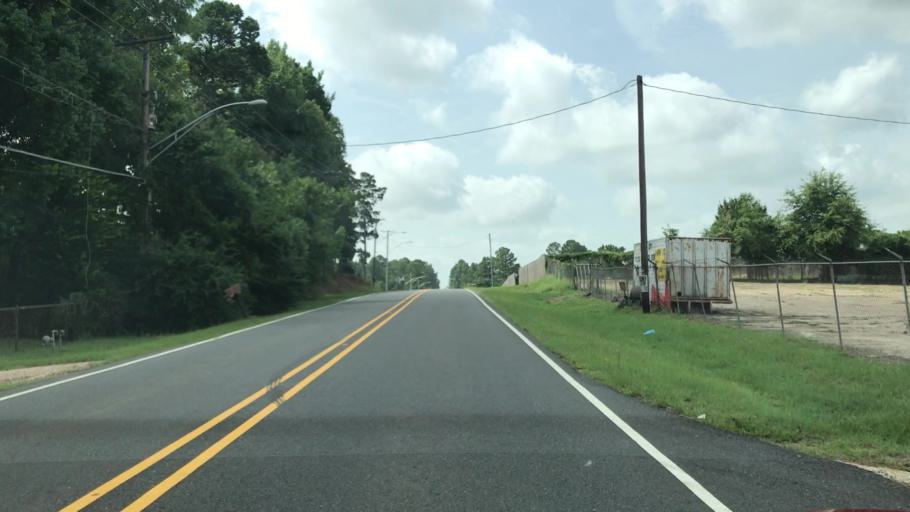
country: US
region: Louisiana
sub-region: De Soto Parish
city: Stonewall
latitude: 32.3892
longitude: -93.7635
